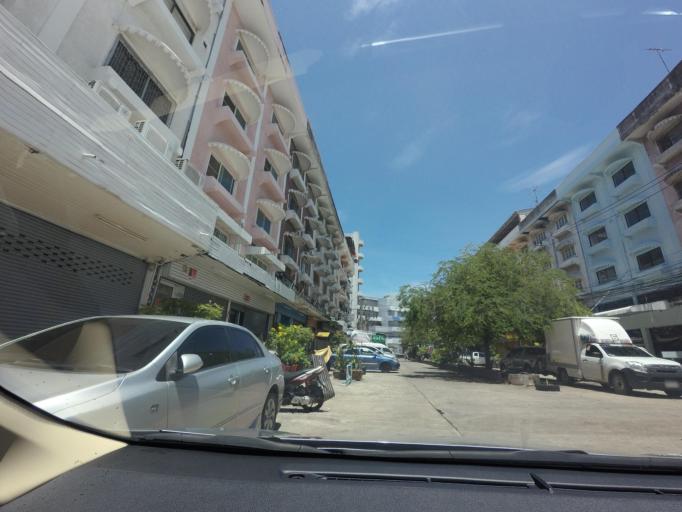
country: TH
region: Bangkok
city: Bang Kapi
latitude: 13.7734
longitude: 100.6299
